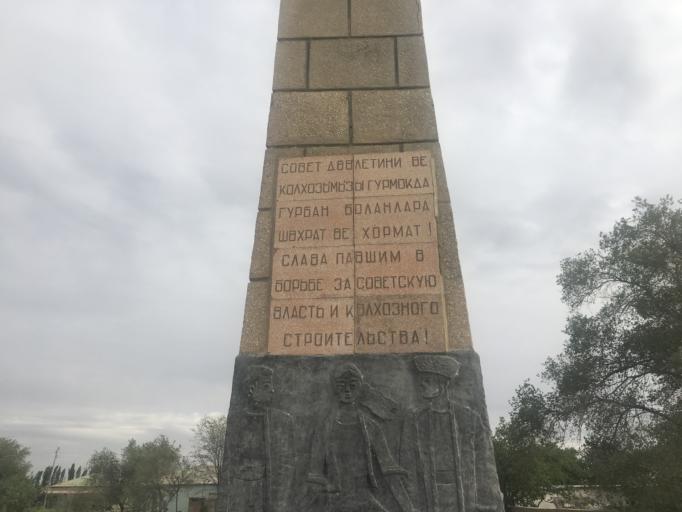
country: TM
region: Dasoguz
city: Dasoguz
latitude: 41.8212
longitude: 59.9117
